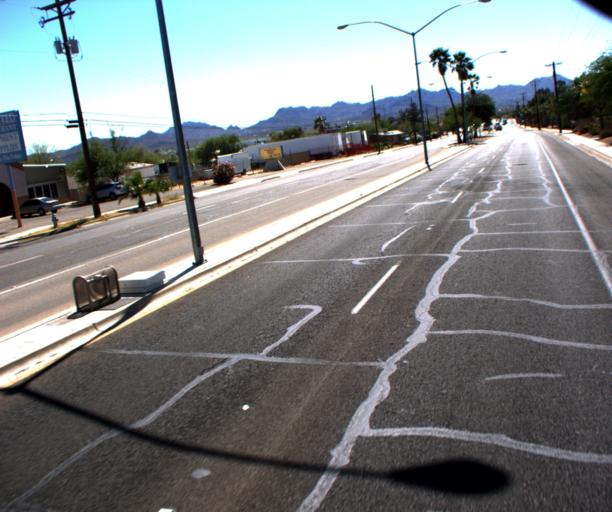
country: US
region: Arizona
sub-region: Pima County
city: Flowing Wells
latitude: 32.2613
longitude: -110.9913
